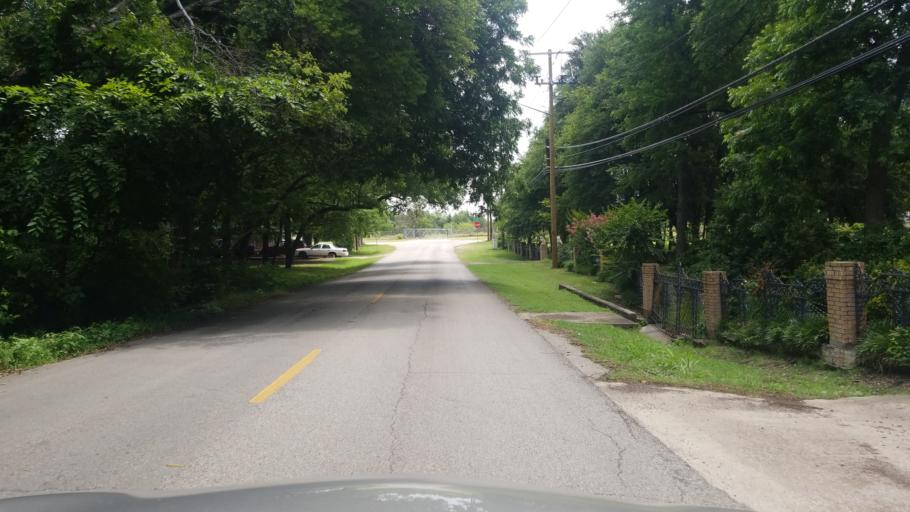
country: US
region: Texas
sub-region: Dallas County
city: Duncanville
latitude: 32.6801
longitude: -96.9099
